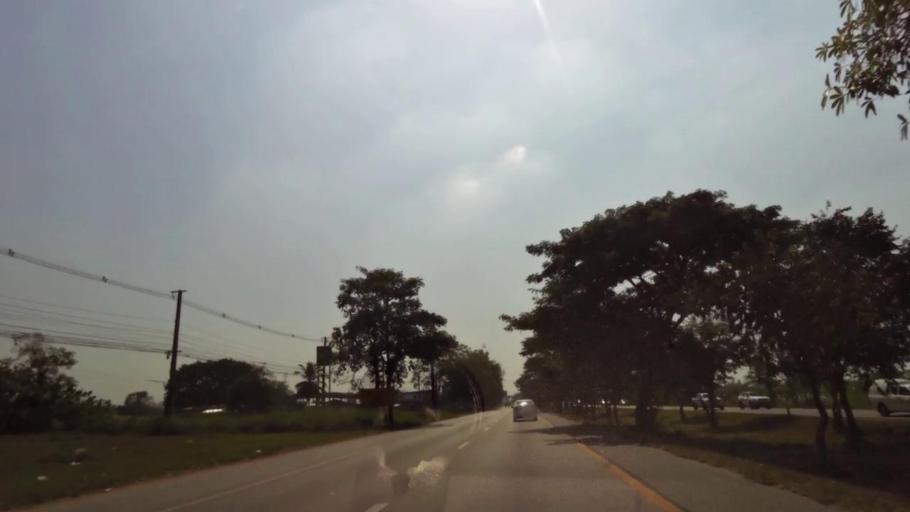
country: TH
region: Phichit
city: Wachira Barami
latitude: 16.5167
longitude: 100.1429
